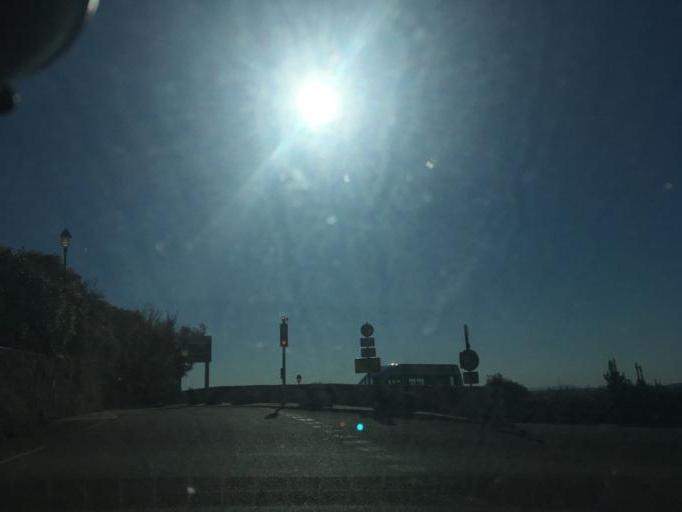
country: FR
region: Provence-Alpes-Cote d'Azur
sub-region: Departement du Var
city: Regusse
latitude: 43.7174
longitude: 6.1346
